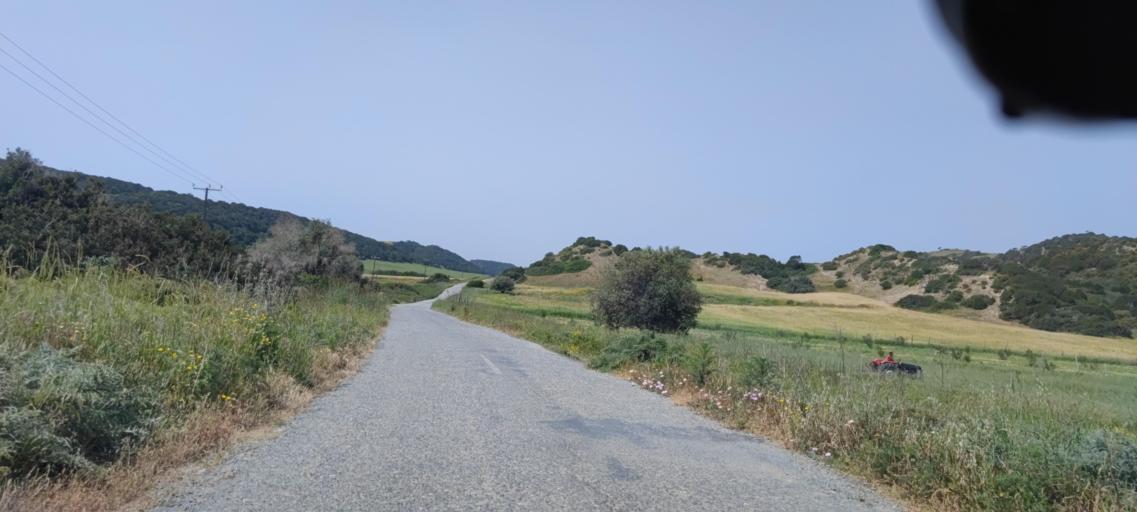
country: CY
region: Ammochostos
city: Rizokarpaso
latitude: 35.6310
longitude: 34.4963
